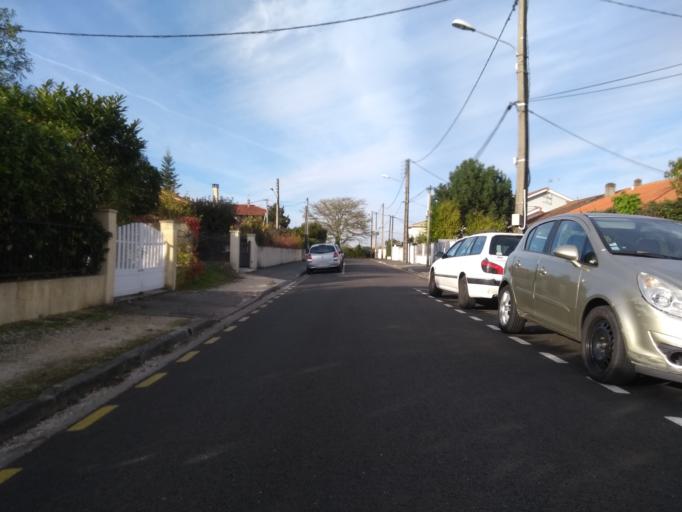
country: FR
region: Aquitaine
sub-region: Departement de la Gironde
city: Pessac
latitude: 44.8029
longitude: -0.6436
